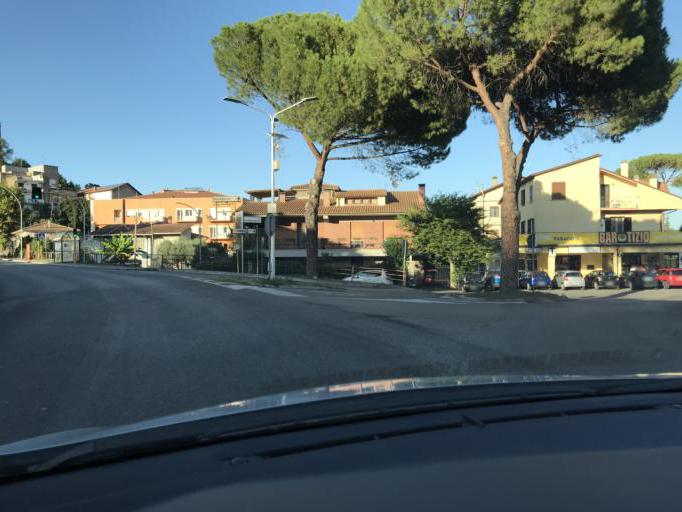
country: IT
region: Latium
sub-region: Provincia di Viterbo
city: Orte
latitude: 42.4563
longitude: 12.3870
